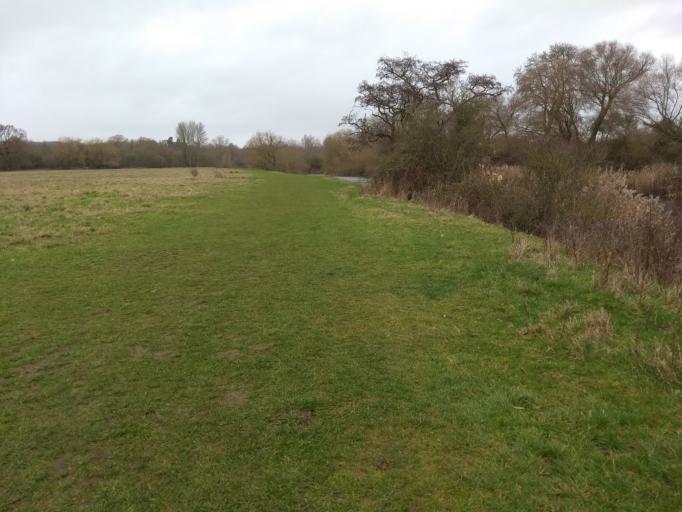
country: GB
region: England
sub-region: Bedford
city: Odell
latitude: 52.2030
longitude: -0.5904
